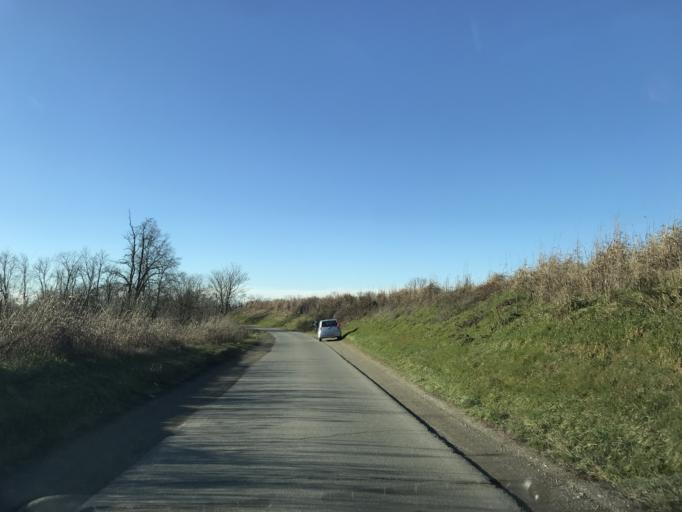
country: IT
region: Lombardy
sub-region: Provincia di Lodi
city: Bargano
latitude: 45.2292
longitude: 9.4575
